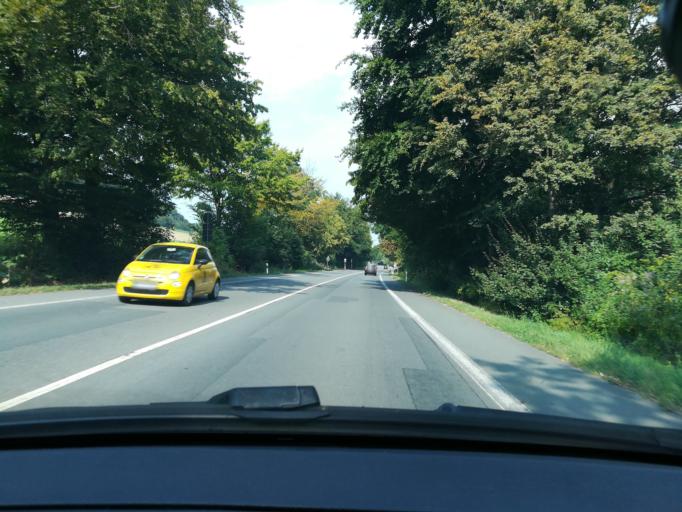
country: DE
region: North Rhine-Westphalia
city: Halle
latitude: 52.0892
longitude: 8.3735
